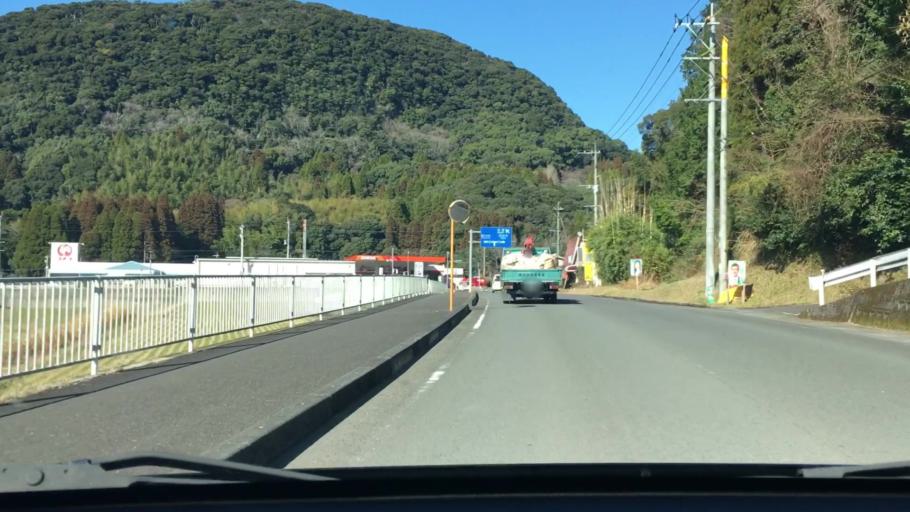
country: JP
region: Kagoshima
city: Satsumasendai
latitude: 31.7962
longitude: 130.4104
